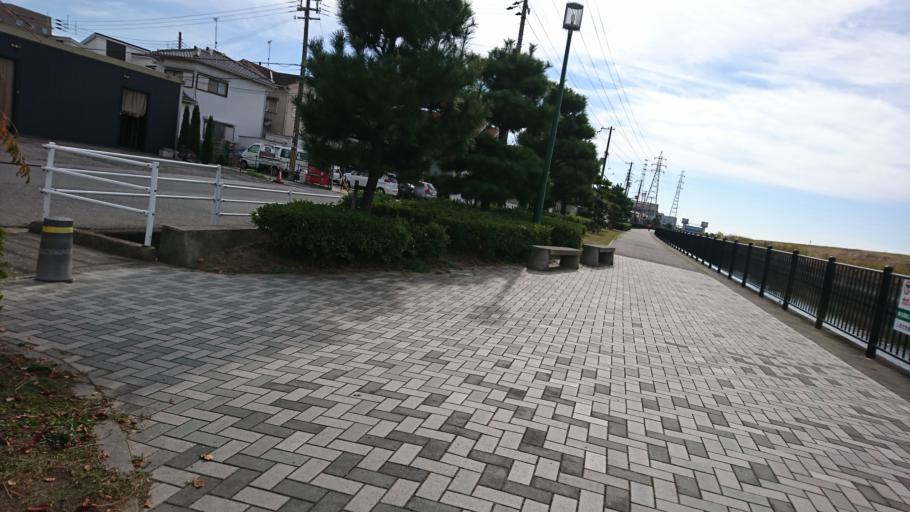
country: JP
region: Hyogo
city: Kakogawacho-honmachi
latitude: 34.7465
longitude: 134.8131
